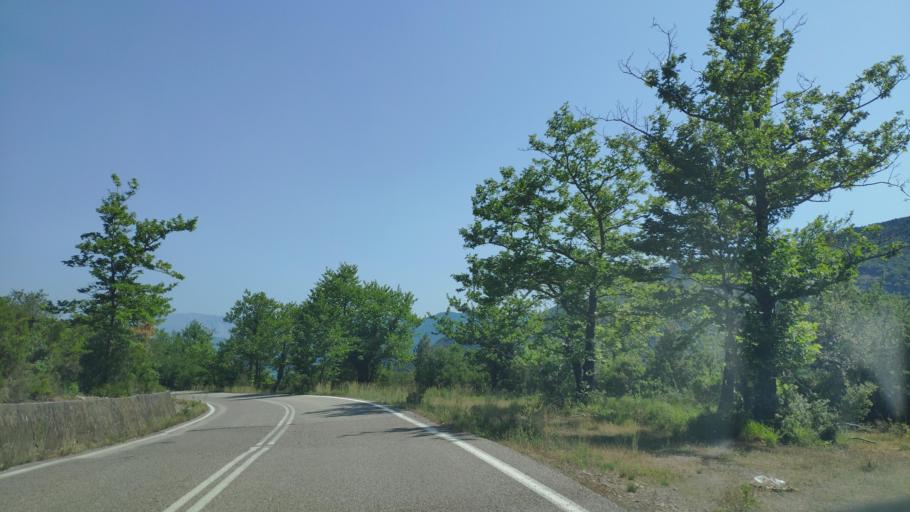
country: GR
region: West Greece
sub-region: Nomos Aitolias kai Akarnanias
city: Lepenou
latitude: 38.7972
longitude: 21.3324
